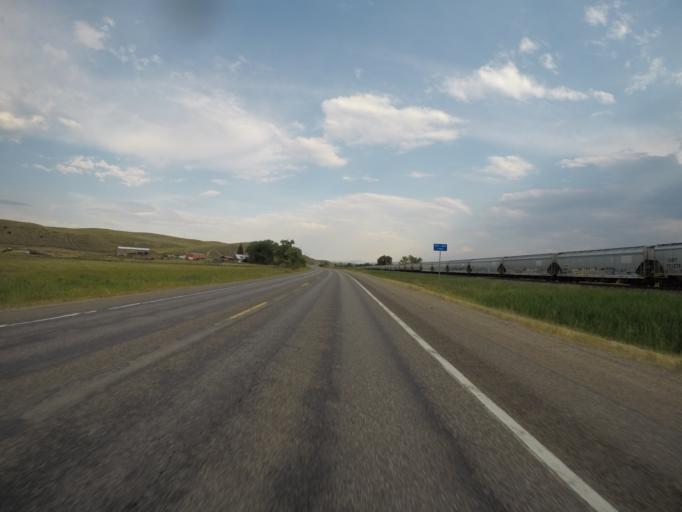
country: US
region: Colorado
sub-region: Routt County
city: Hayden
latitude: 40.5129
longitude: -107.3892
